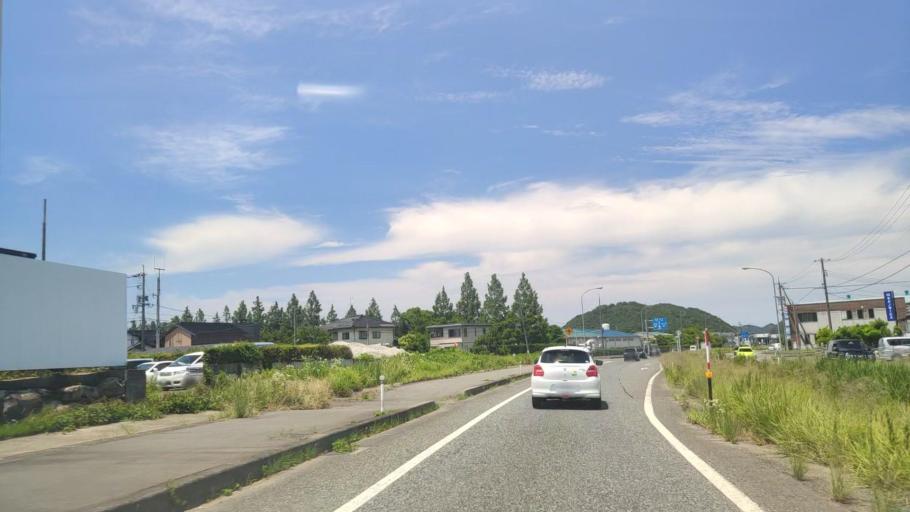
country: JP
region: Tottori
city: Tottori
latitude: 35.4548
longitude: 134.2435
